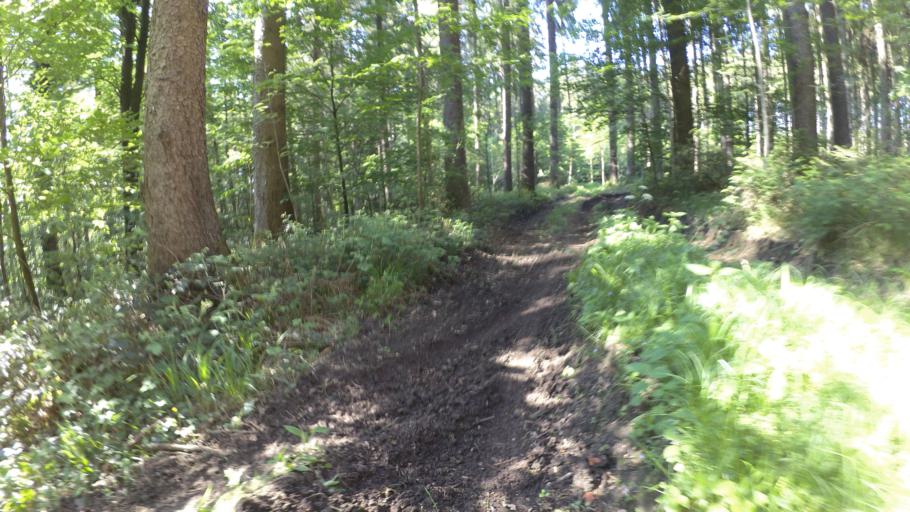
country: DE
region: Bavaria
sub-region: Upper Bavaria
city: Seeon-Seebruck
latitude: 47.9314
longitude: 12.4982
